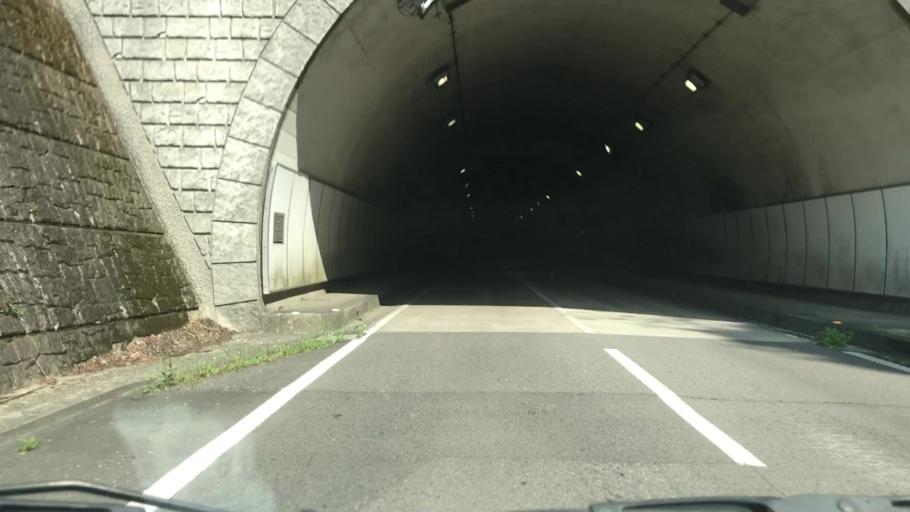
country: JP
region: Saga Prefecture
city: Takeocho-takeo
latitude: 33.2138
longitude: 130.0066
